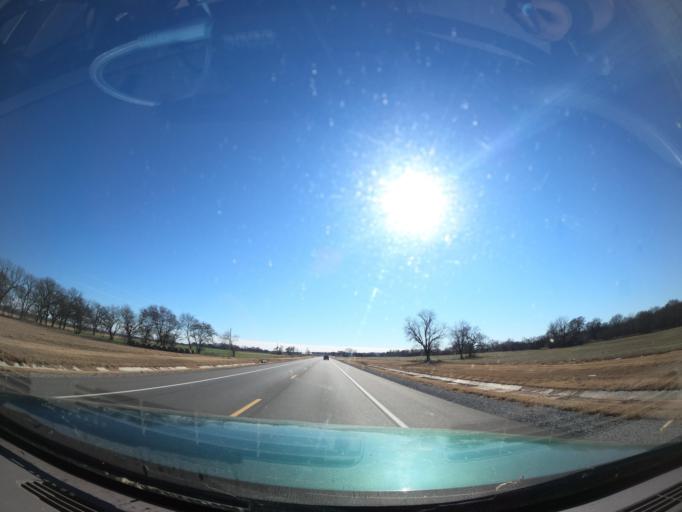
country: US
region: Oklahoma
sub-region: Wagoner County
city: Coweta
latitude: 35.8939
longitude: -95.6592
